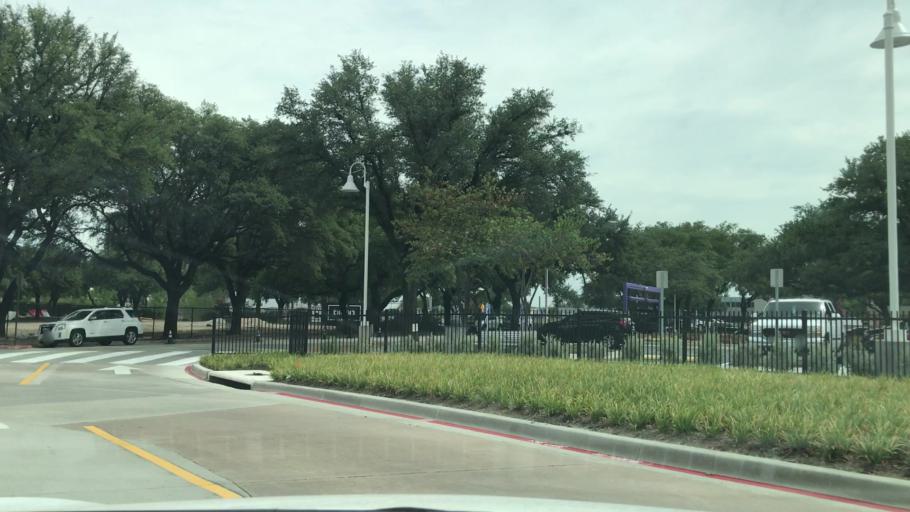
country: US
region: Texas
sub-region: Dallas County
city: Dallas
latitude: 32.8062
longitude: -96.8363
